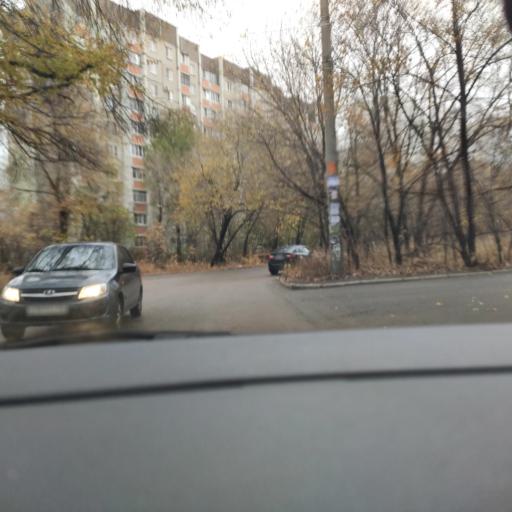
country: RU
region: Voronezj
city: Voronezh
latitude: 51.6827
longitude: 39.1300
